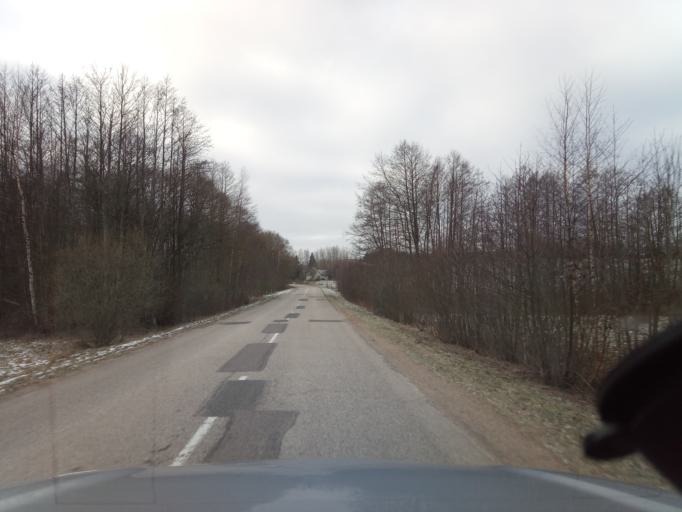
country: LT
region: Alytaus apskritis
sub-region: Alytaus rajonas
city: Daugai
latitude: 54.3462
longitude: 24.3146
